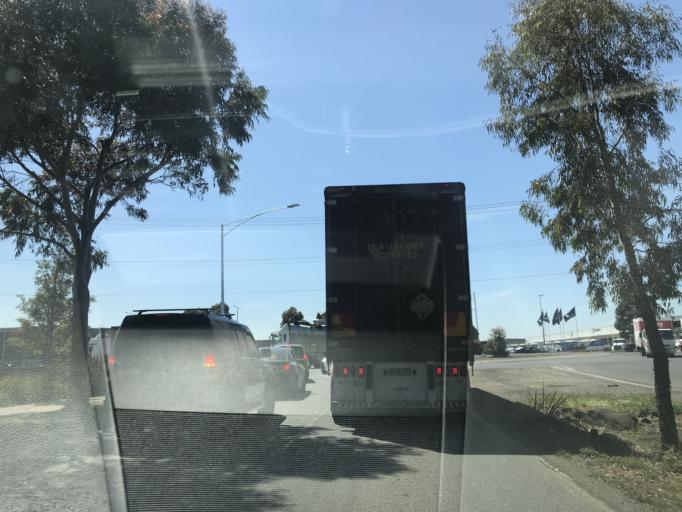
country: AU
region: Victoria
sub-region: Wyndham
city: Truganina
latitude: -37.8124
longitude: 144.7657
